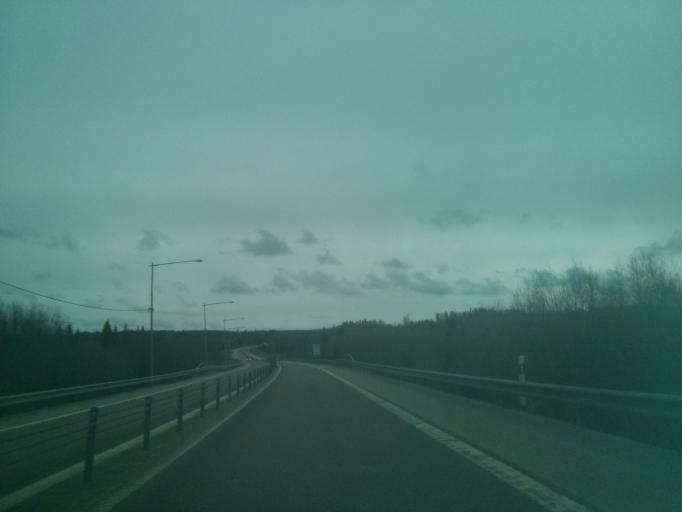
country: SE
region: Vaesternorrland
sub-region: Timra Kommun
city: Soraker
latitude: 62.5214
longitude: 17.4704
